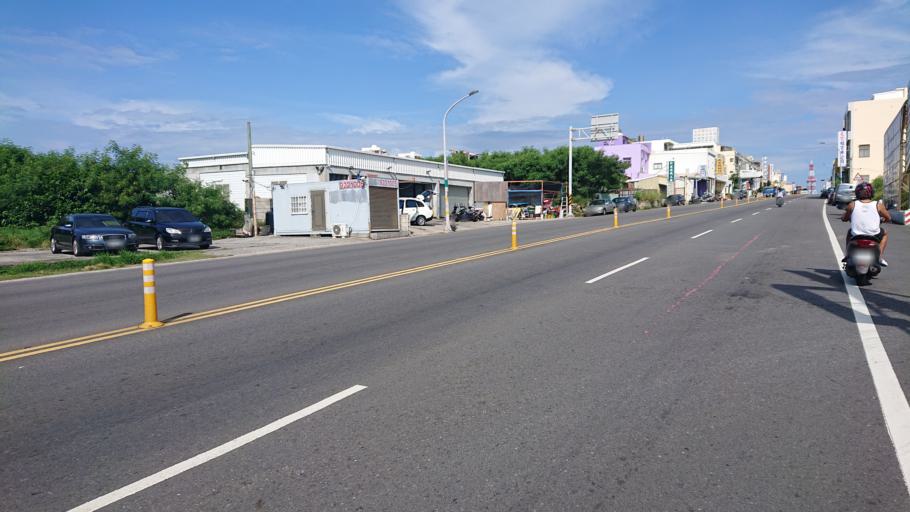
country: TW
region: Taiwan
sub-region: Penghu
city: Ma-kung
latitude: 23.5644
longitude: 119.5881
